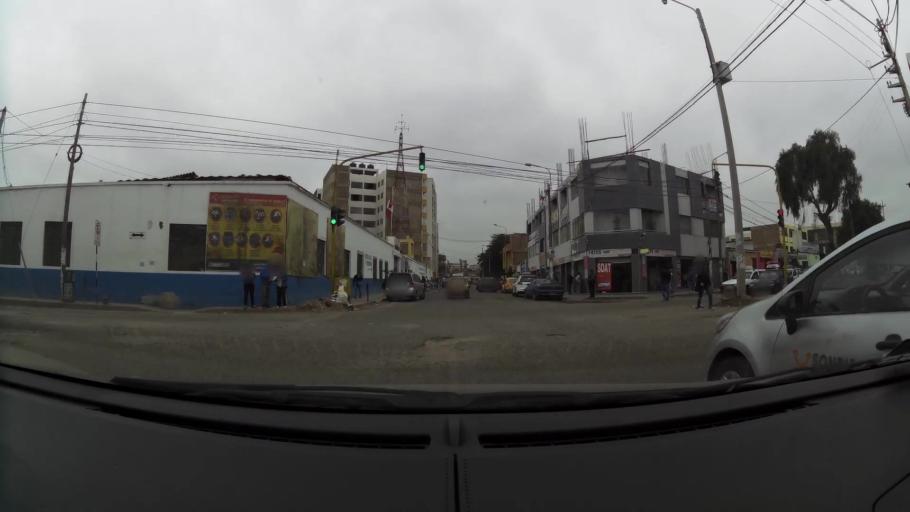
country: PE
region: La Libertad
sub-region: Provincia de Trujillo
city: Trujillo
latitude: -8.1181
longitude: -79.0249
